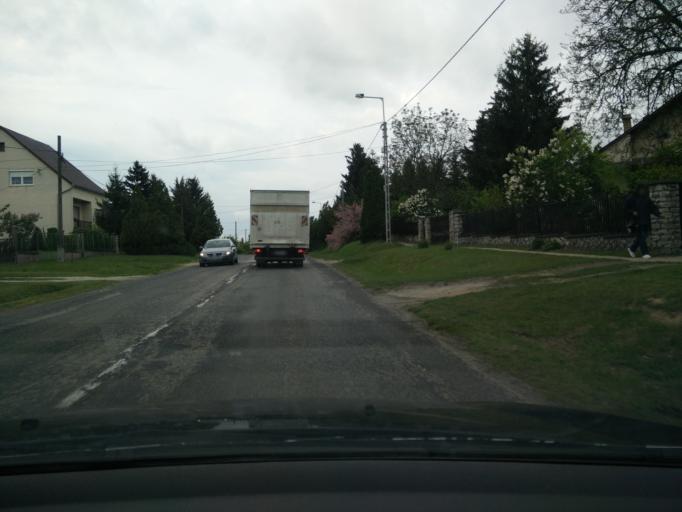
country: HU
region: Gyor-Moson-Sopron
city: Gyorszemere
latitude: 47.5468
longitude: 17.5550
